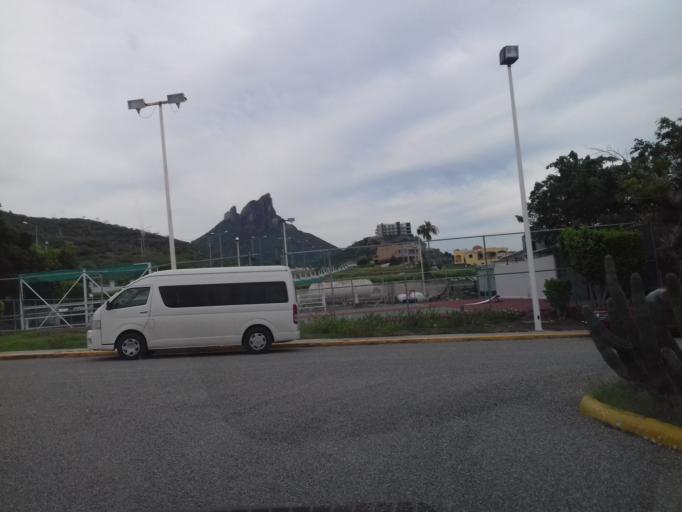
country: MX
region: Sonora
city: Heroica Guaymas
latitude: 27.9603
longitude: -111.0961
